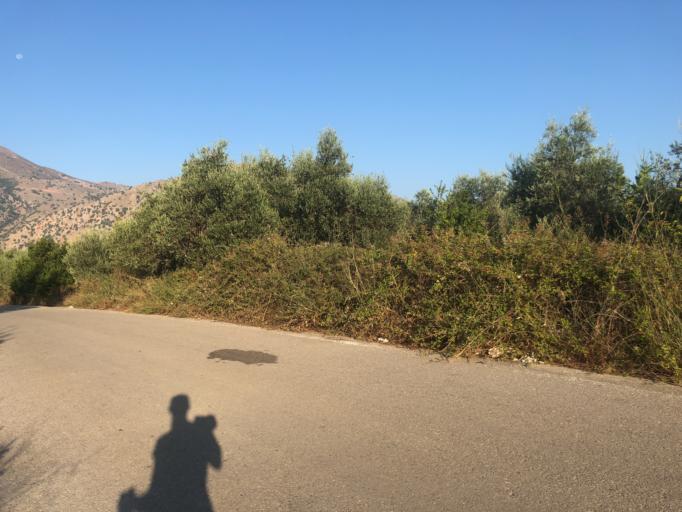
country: GR
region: Crete
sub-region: Nomos Chanias
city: Georgioupolis
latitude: 35.3388
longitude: 24.2895
